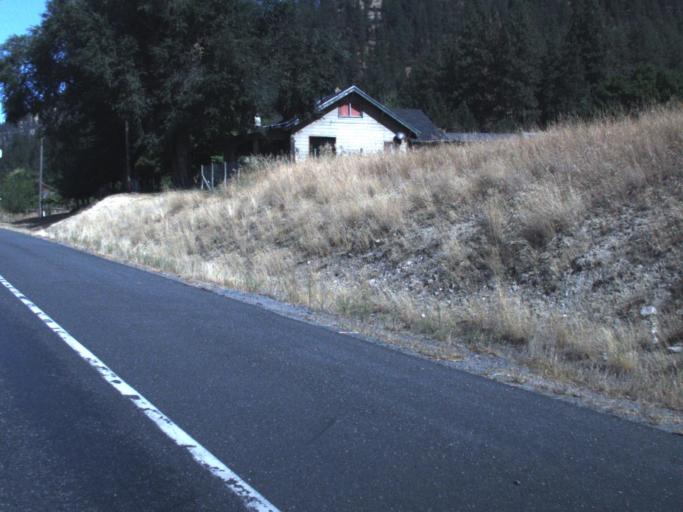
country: US
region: Washington
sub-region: Stevens County
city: Chewelah
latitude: 48.3544
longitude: -117.8341
